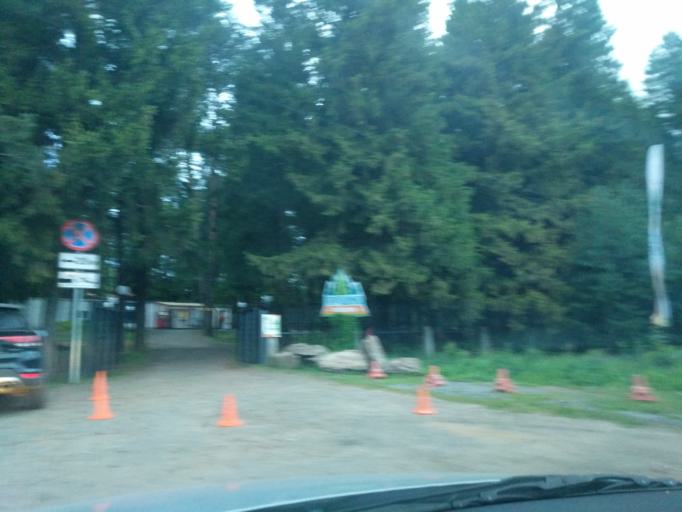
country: RU
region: Kirov
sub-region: Kirovo-Chepetskiy Rayon
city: Kirov
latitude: 58.6062
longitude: 49.8106
